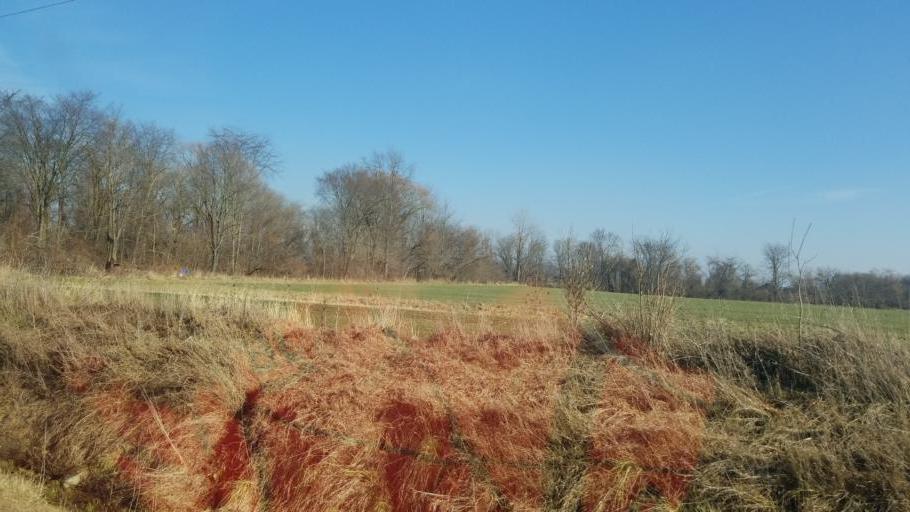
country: US
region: Ohio
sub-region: Seneca County
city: Tiffin
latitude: 41.0350
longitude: -83.0740
